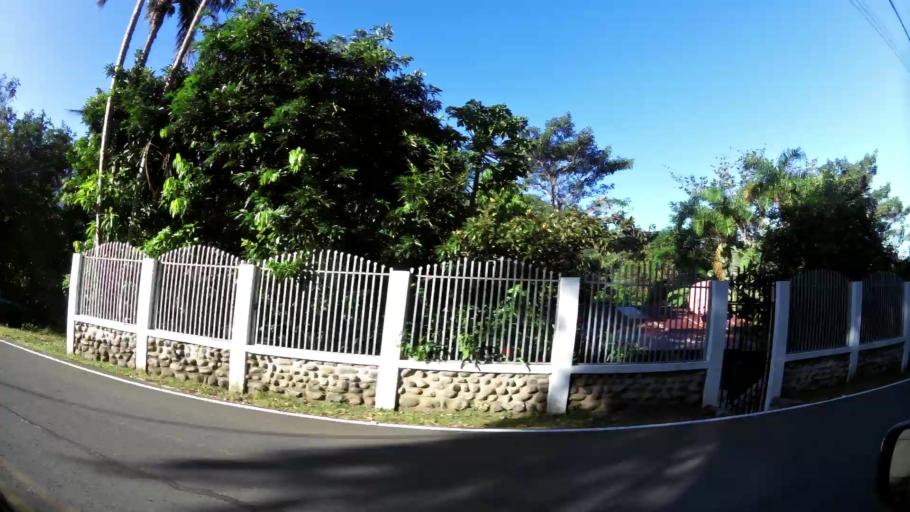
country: CR
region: Guanacaste
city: Juntas
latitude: 10.2065
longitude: -84.8475
